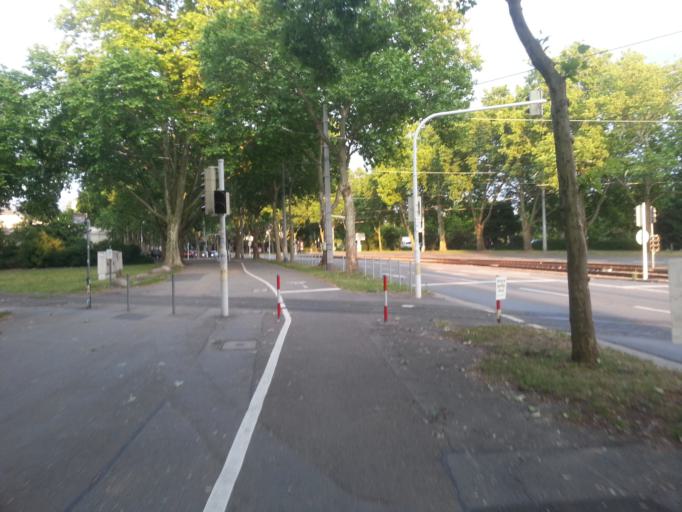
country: DE
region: Baden-Wuerttemberg
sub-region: Karlsruhe Region
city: Mannheim
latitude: 49.4785
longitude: 8.4974
